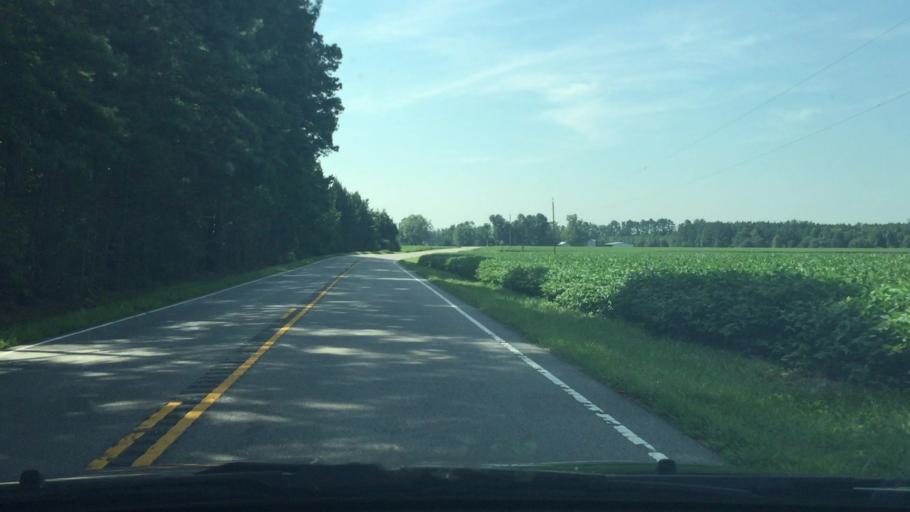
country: US
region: Virginia
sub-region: Southampton County
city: Courtland
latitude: 36.8477
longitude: -77.1329
